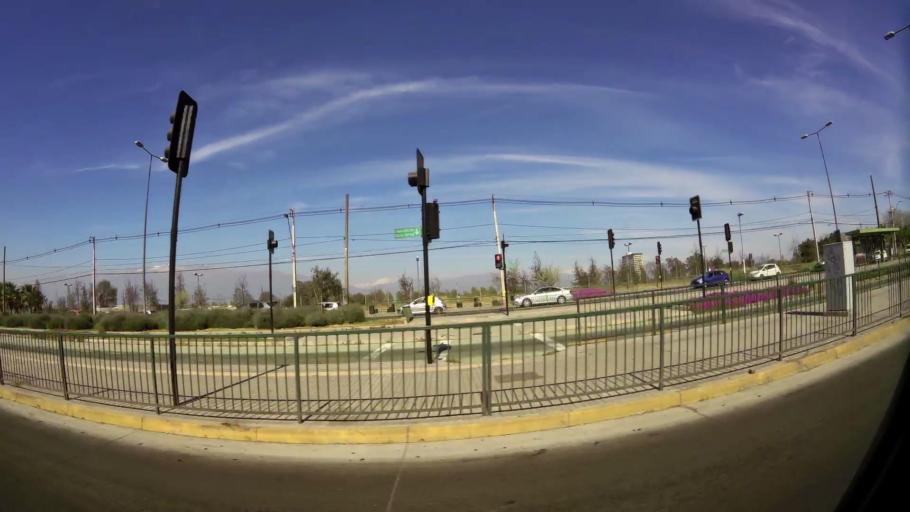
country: CL
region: Santiago Metropolitan
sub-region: Provincia de Santiago
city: Lo Prado
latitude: -33.5002
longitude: -70.7092
